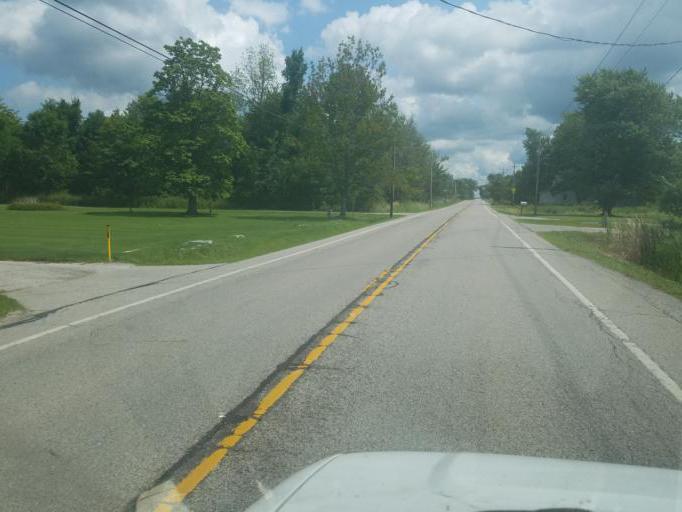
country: US
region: Ohio
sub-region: Ashtabula County
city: Roaming Shores
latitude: 41.6055
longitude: -80.8487
